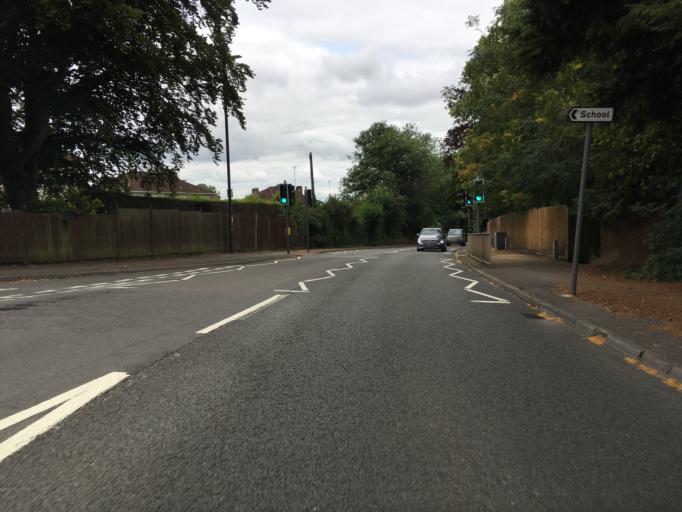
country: GB
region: England
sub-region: Gloucestershire
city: Charlton Kings
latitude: 51.8844
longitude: -2.0464
